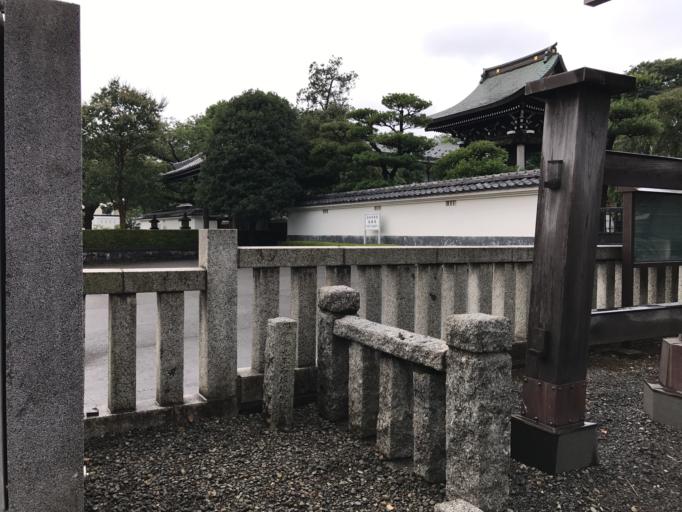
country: JP
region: Tokyo
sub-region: Machida-shi
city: Machida
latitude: 35.5385
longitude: 139.4445
